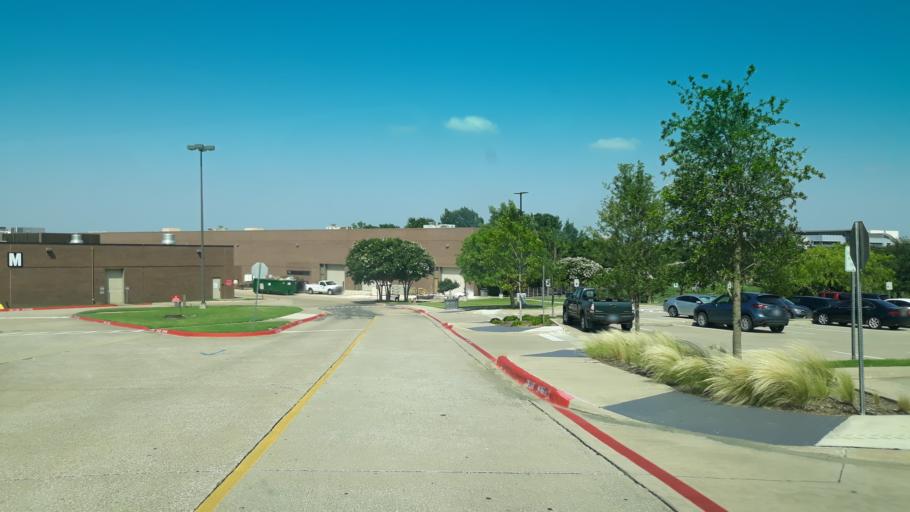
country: US
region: Texas
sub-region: Dallas County
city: Irving
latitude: 32.8695
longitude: -96.9683
